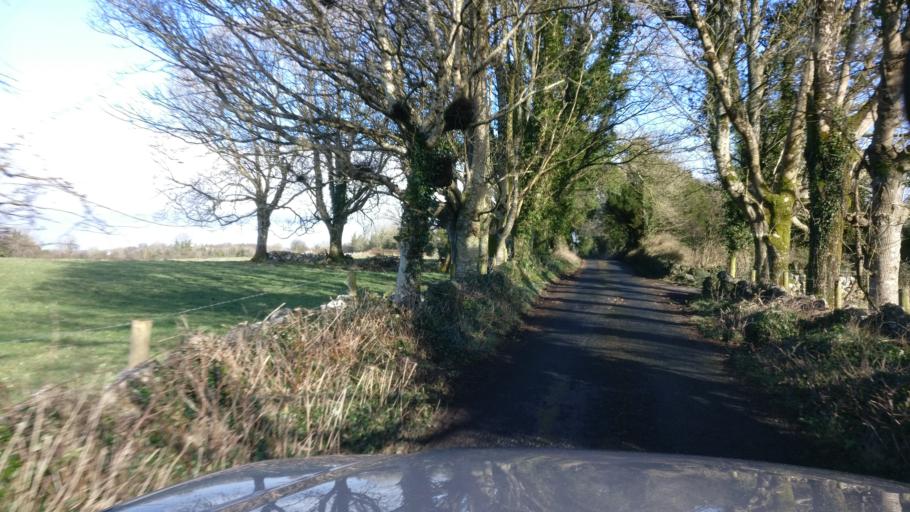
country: IE
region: Connaught
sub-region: County Galway
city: Loughrea
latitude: 53.2153
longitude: -8.6677
